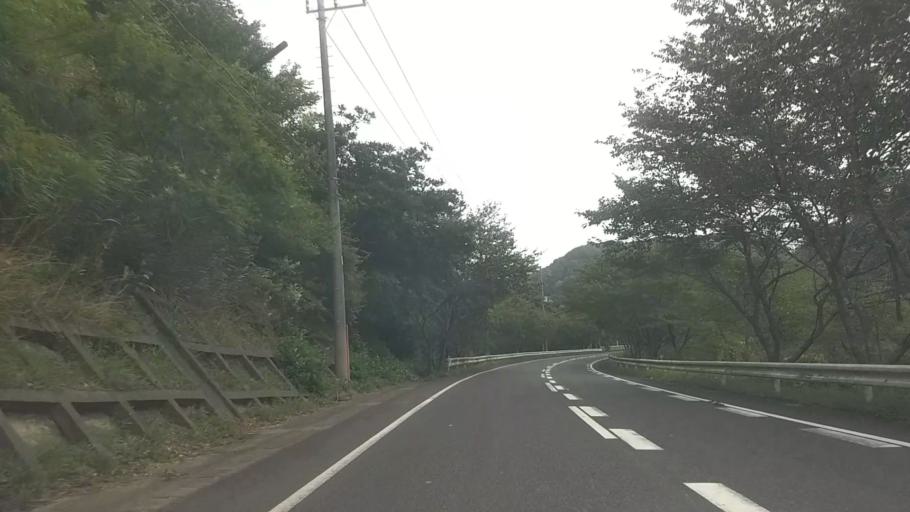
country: JP
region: Chiba
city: Kimitsu
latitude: 35.2351
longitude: 139.9696
